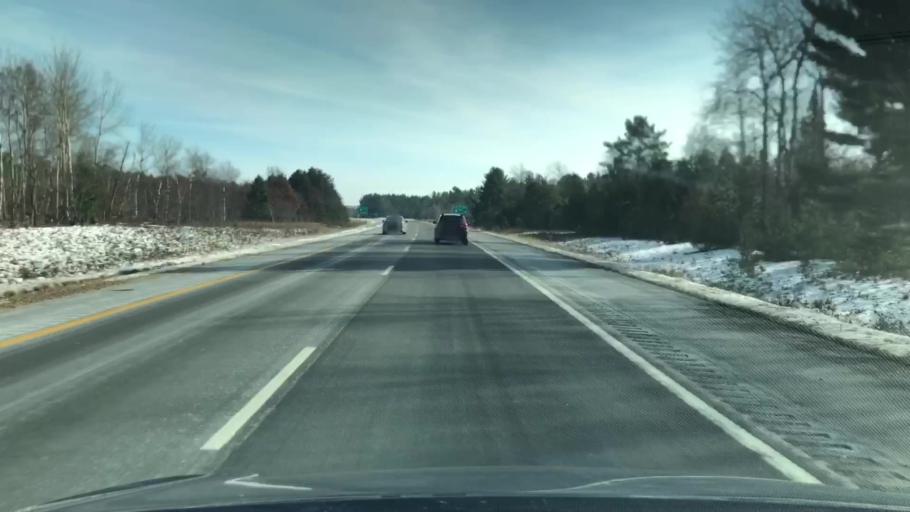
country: US
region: Michigan
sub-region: Roscommon County
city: Saint Helen
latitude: 44.3169
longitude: -84.5181
